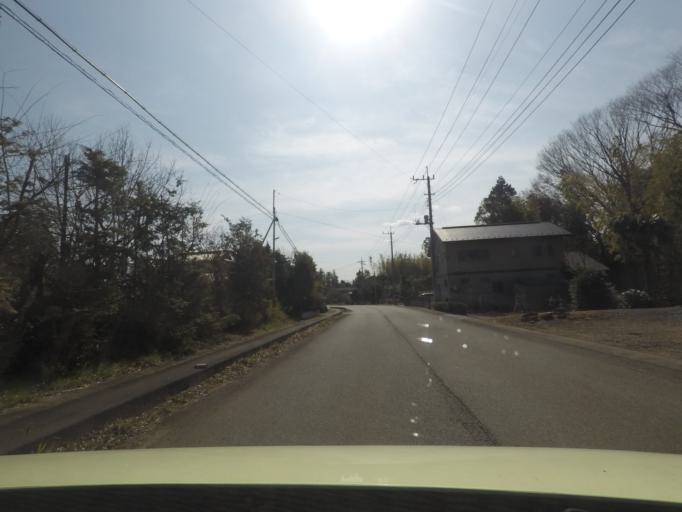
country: JP
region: Ibaraki
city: Ishioka
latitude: 36.2013
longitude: 140.3214
